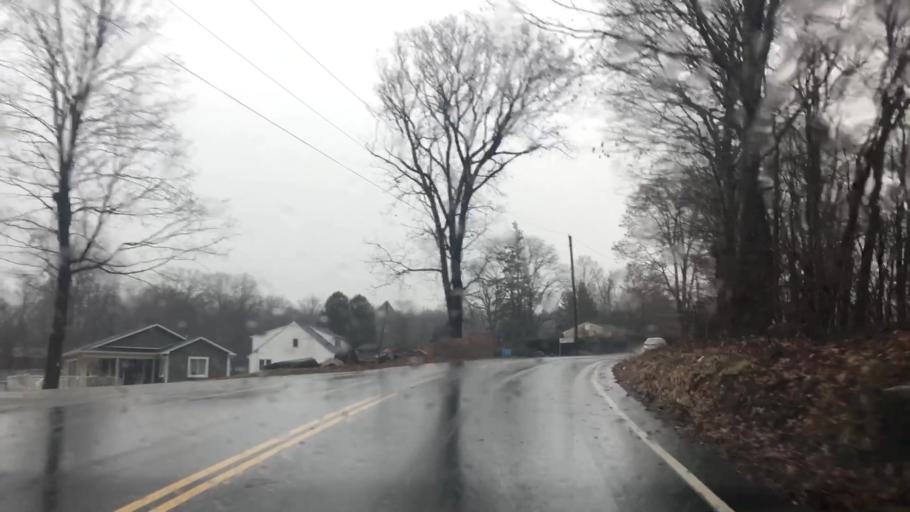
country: US
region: New York
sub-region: Putnam County
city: Putnam Lake
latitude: 41.4573
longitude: -73.5424
